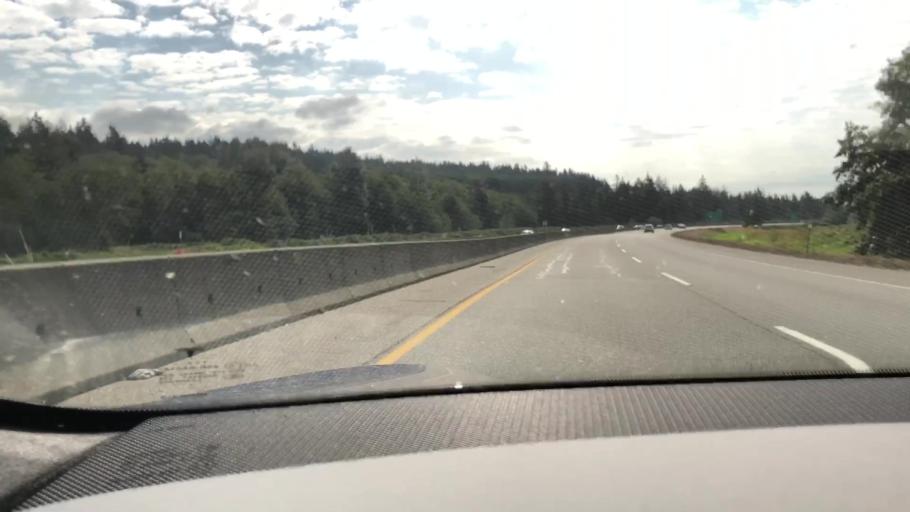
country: CA
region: British Columbia
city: Delta
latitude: 49.1124
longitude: -122.9090
